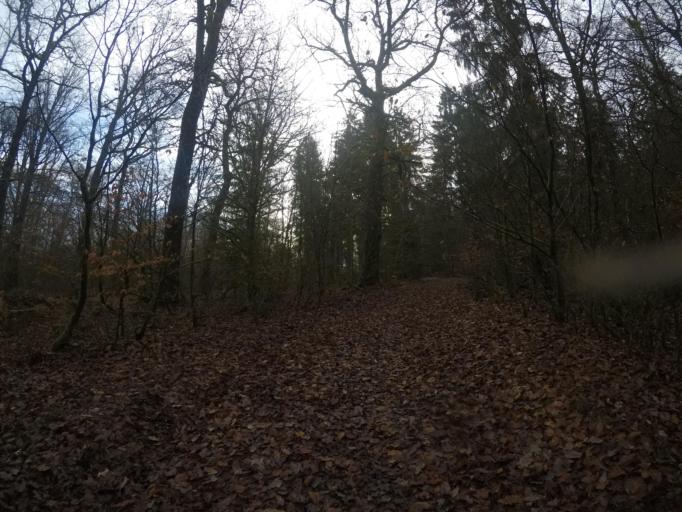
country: BE
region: Wallonia
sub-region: Province du Luxembourg
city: Habay-la-Vieille
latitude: 49.7578
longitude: 5.6000
